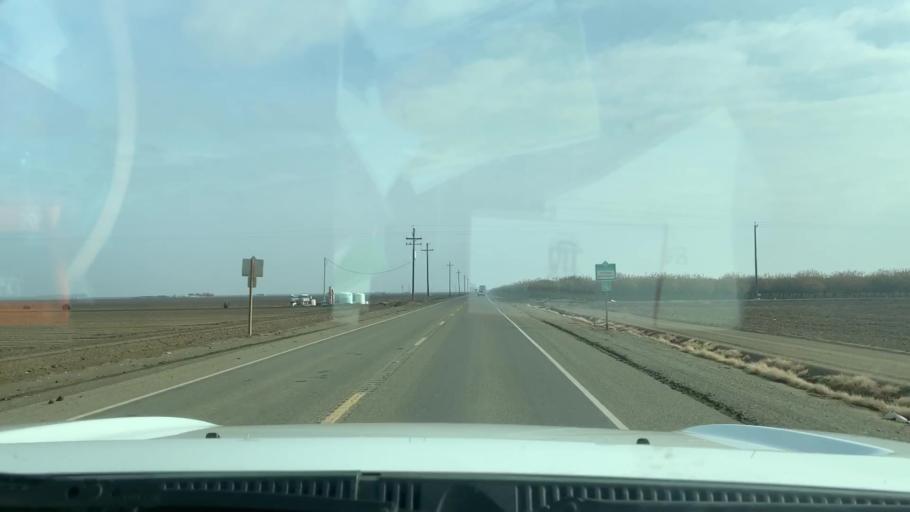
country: US
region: California
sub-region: Kings County
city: Lemoore Station
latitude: 36.2554
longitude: -119.9781
